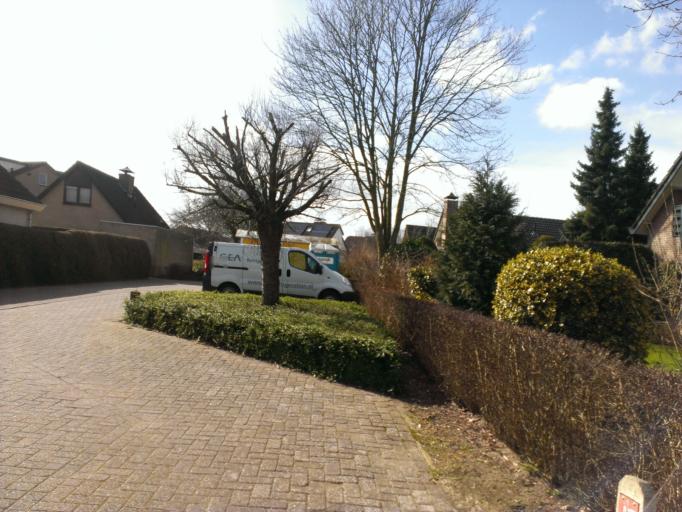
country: NL
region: Gelderland
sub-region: Gemeente Voorst
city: Twello
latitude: 52.2296
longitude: 6.1039
